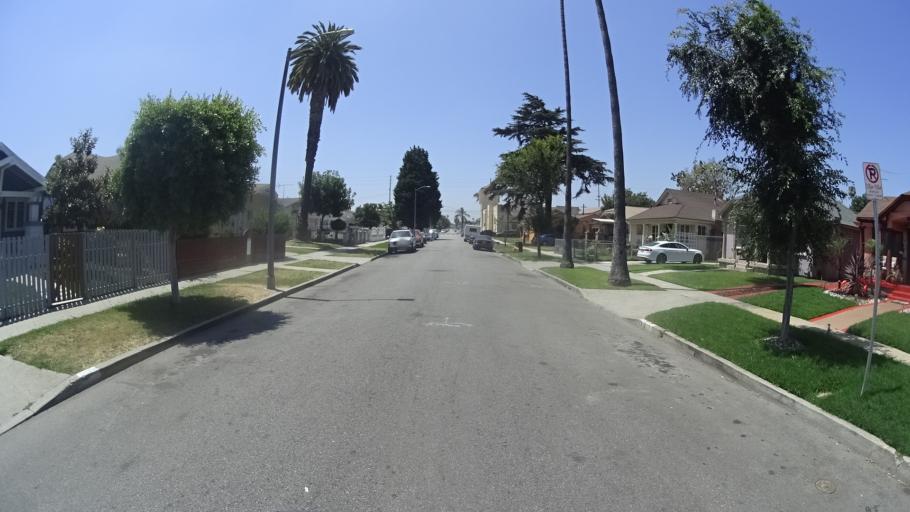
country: US
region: California
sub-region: Los Angeles County
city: View Park-Windsor Hills
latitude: 33.9945
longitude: -118.3236
